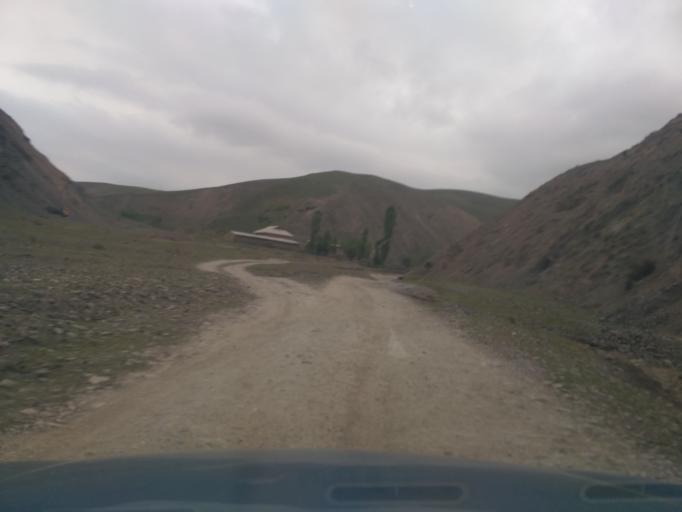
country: UZ
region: Jizzax
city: Zomin
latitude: 39.8467
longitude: 68.3996
